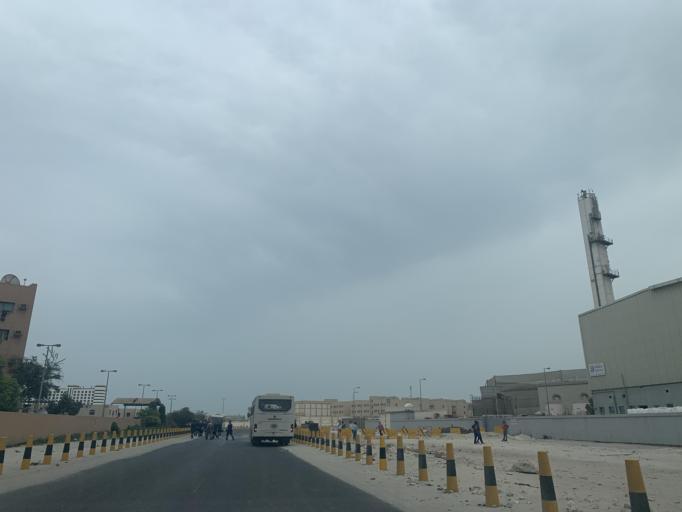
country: BH
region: Muharraq
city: Al Hadd
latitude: 26.2087
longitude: 50.6770
